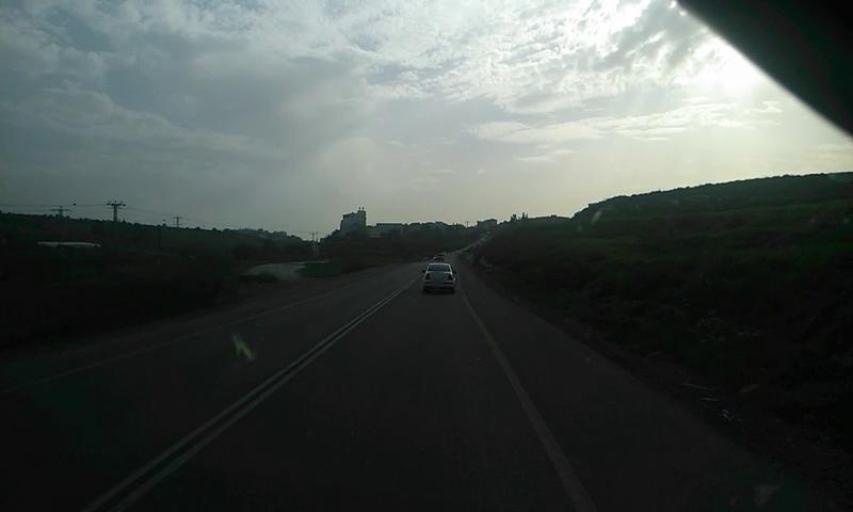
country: PS
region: West Bank
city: Hajjah
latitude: 32.1945
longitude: 35.1419
